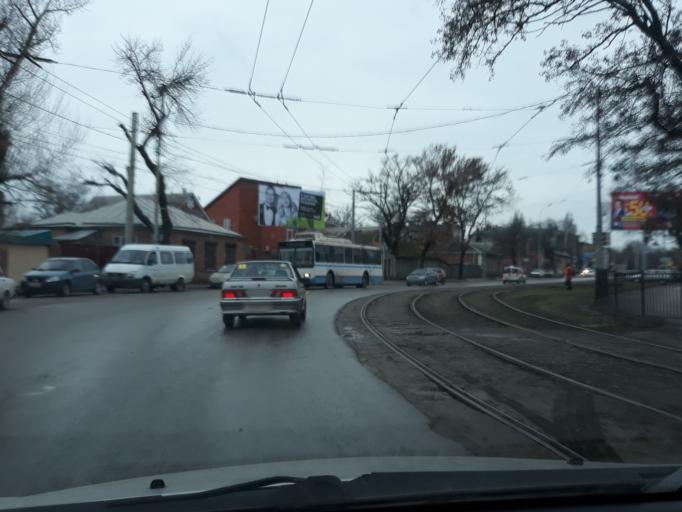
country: RU
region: Rostov
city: Taganrog
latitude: 47.2246
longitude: 38.9181
